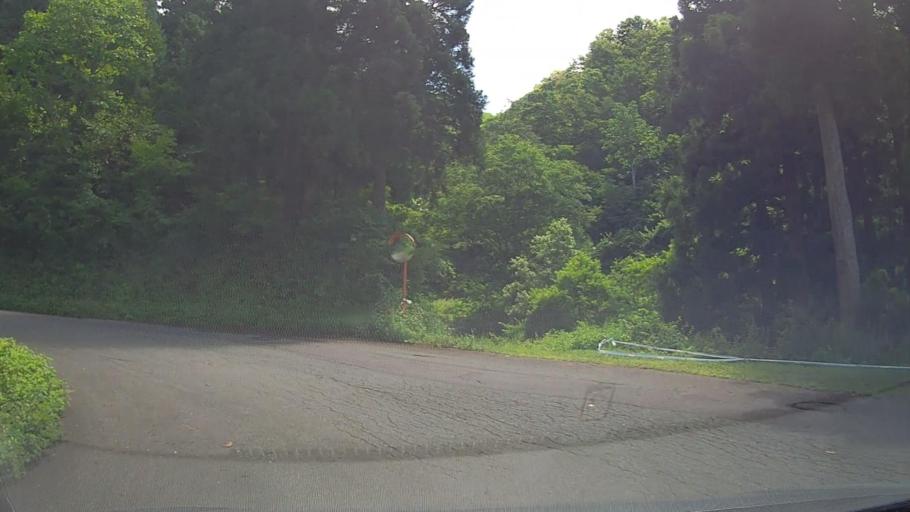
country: JP
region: Nagano
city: Iiyama
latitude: 36.9307
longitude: 138.4651
